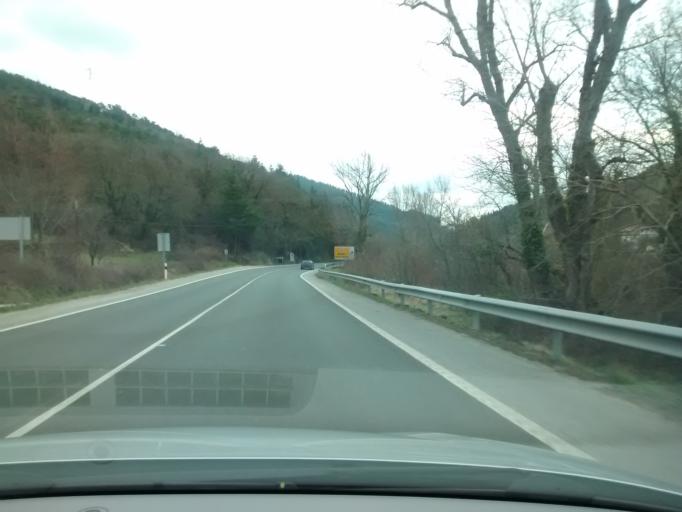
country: ES
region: Basque Country
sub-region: Bizkaia
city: Balmaseda
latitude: 43.1676
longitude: -3.2287
